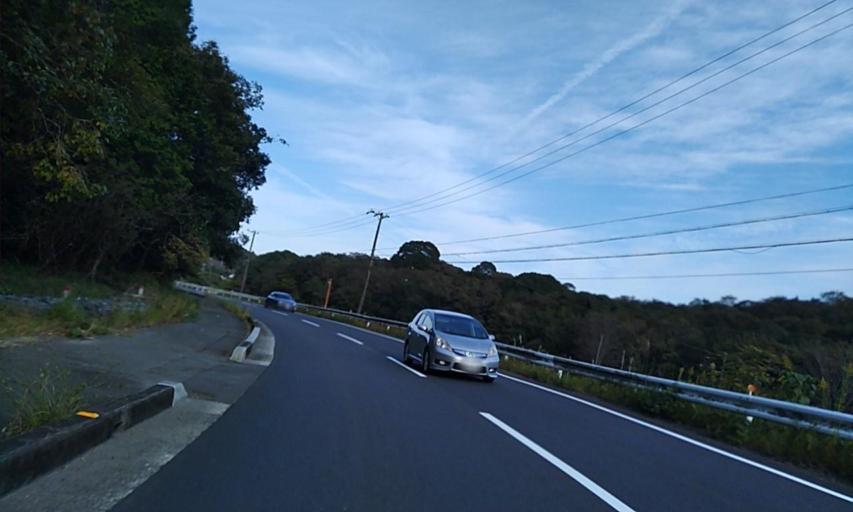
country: JP
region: Mie
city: Ise
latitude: 34.3556
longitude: 136.7529
